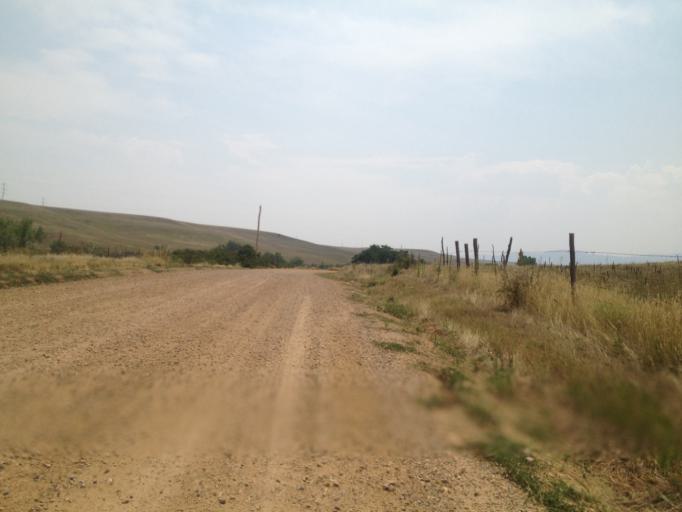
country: US
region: Colorado
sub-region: Boulder County
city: Superior
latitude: 39.9455
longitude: -105.1869
